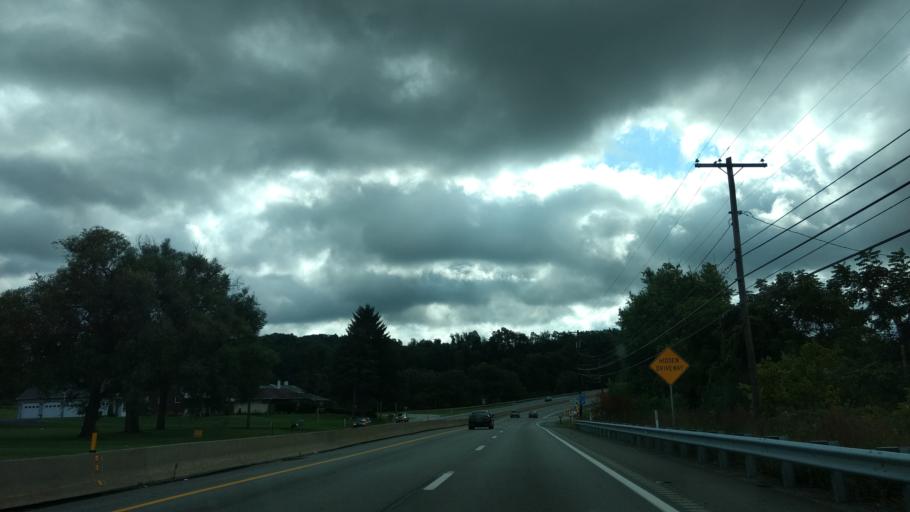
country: US
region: Pennsylvania
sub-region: Westmoreland County
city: Fellsburg
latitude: 40.1830
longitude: -79.8087
